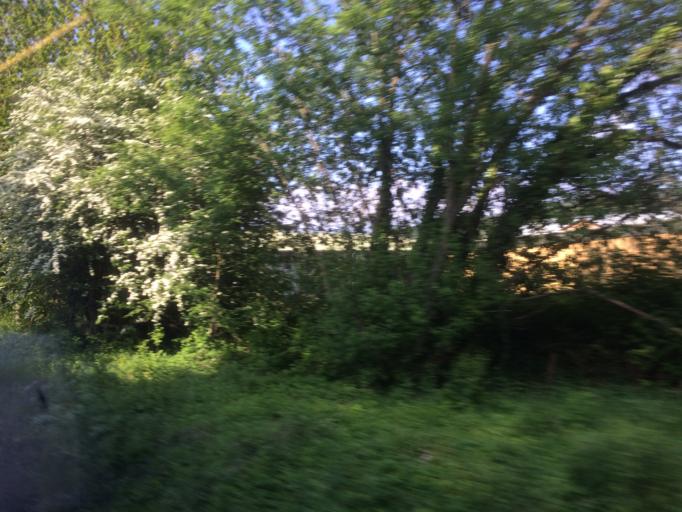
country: GB
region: Scotland
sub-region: Perth and Kinross
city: Perth
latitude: 56.3783
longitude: -3.4299
